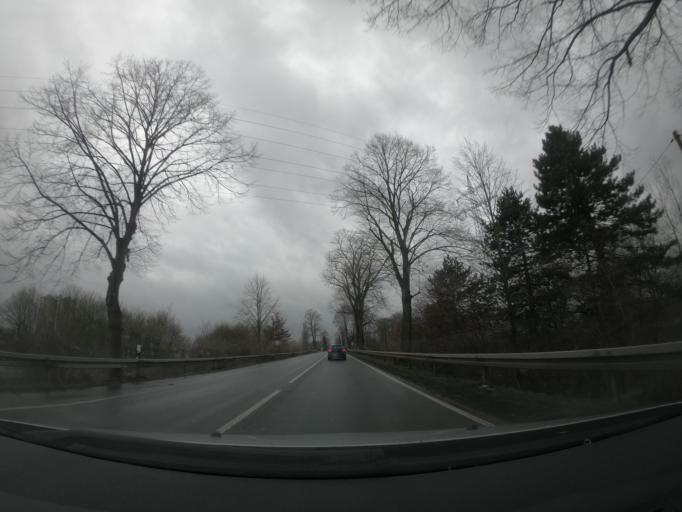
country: DE
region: North Rhine-Westphalia
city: Waltrop
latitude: 51.5865
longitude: 7.4059
